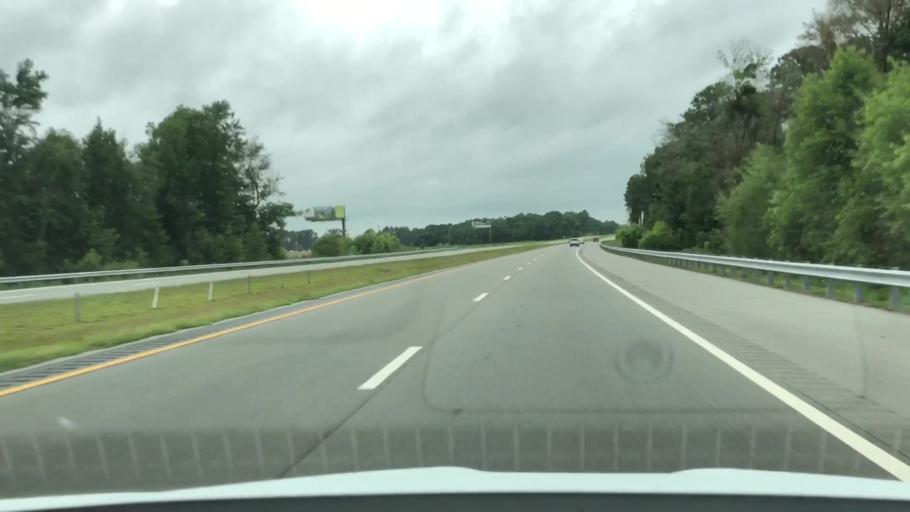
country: US
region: North Carolina
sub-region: Lenoir County
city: La Grange
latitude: 35.3296
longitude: -77.8415
